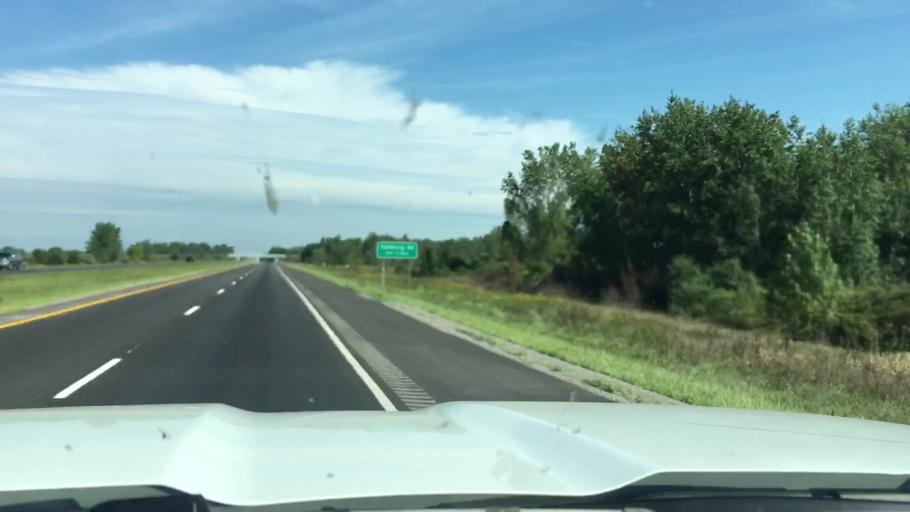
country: US
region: Michigan
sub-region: Saginaw County
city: Freeland
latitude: 43.5598
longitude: -84.1390
